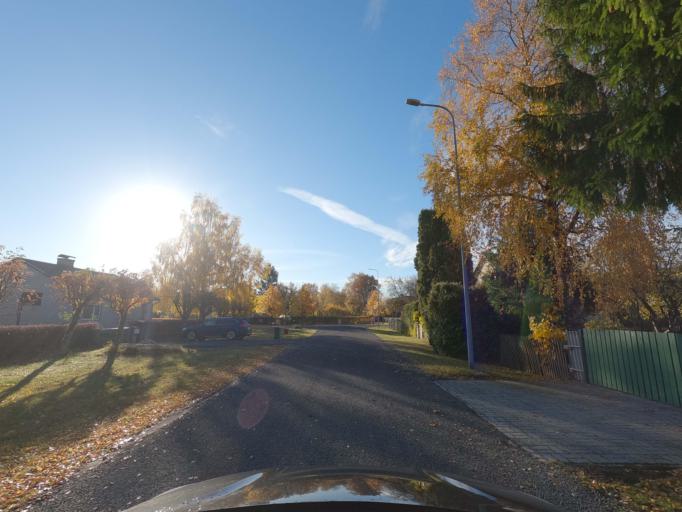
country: EE
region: Raplamaa
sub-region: Kohila vald
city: Kohila
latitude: 59.1630
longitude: 24.7681
